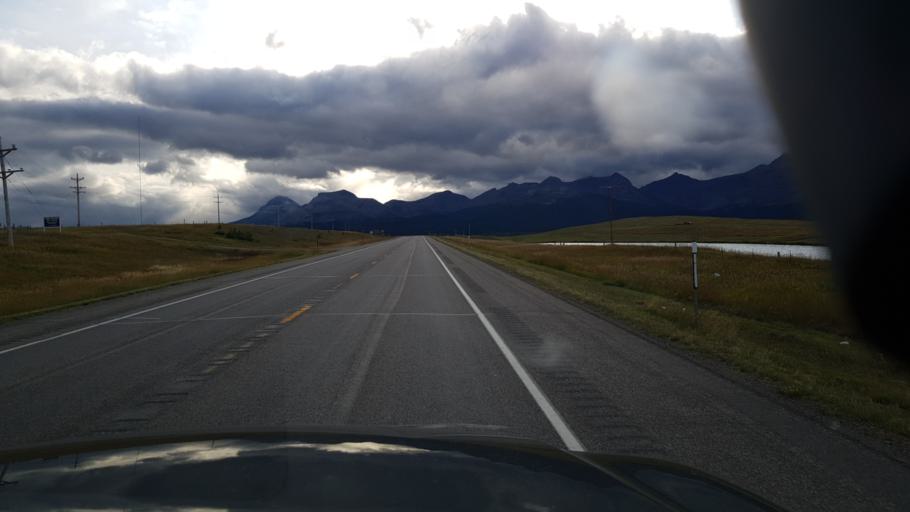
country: US
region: Montana
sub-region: Glacier County
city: South Browning
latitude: 48.4555
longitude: -113.1863
